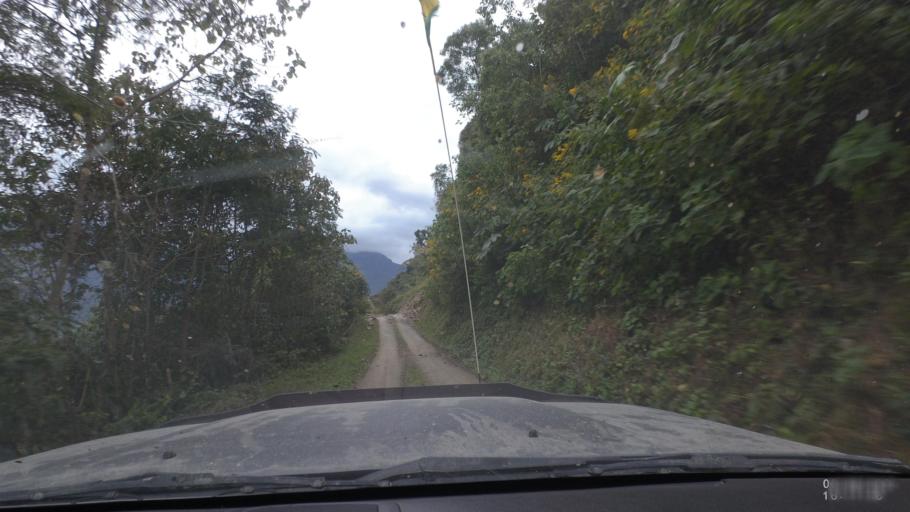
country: BO
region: La Paz
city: Quime
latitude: -16.5502
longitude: -66.7393
